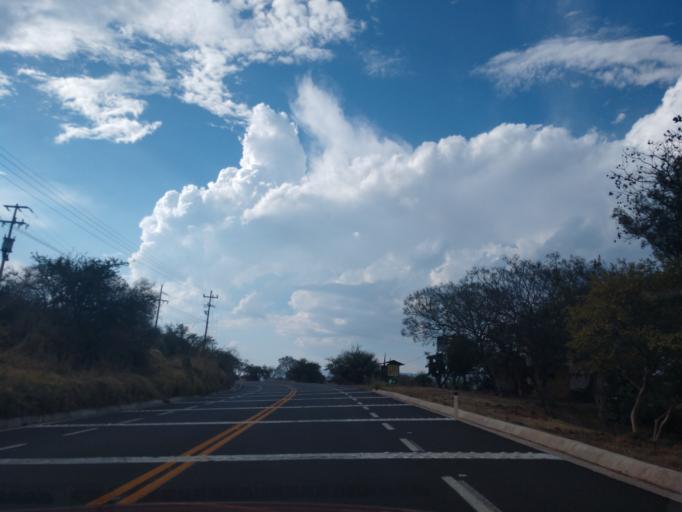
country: MX
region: Jalisco
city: Ajijic
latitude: 20.1887
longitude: -103.2548
